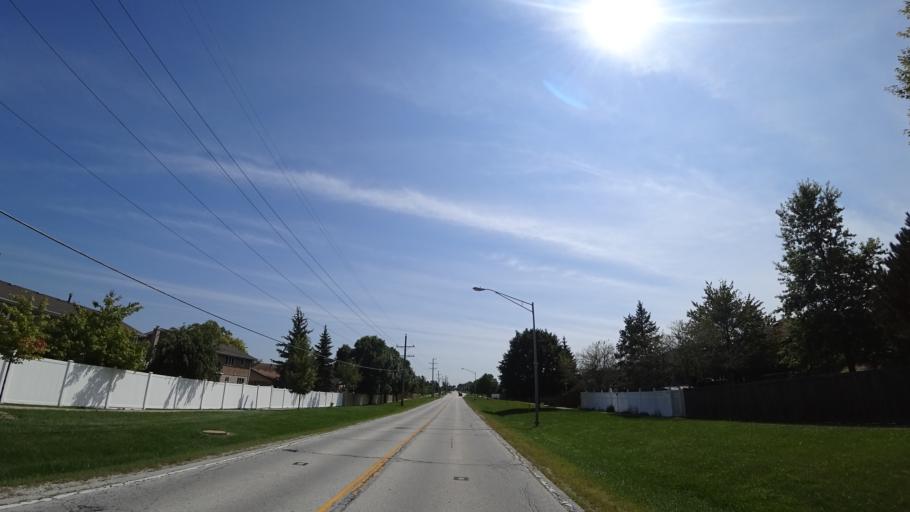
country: US
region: Illinois
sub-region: Cook County
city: Orland Hills
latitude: 41.5683
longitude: -87.8467
